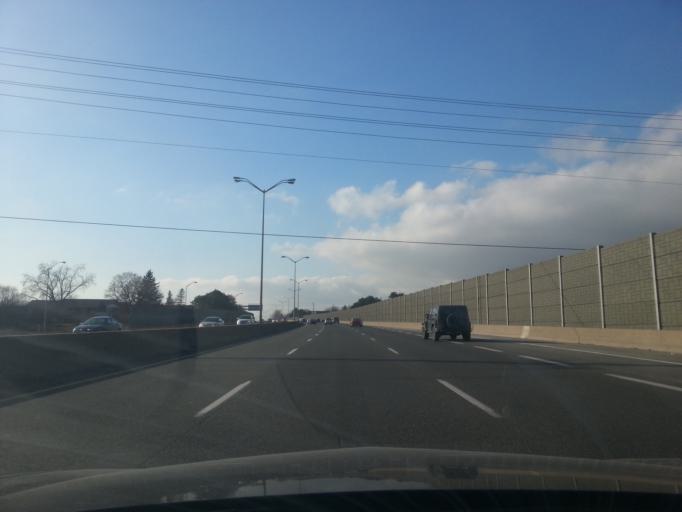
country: CA
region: Ontario
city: Oshawa
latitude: 43.8870
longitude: -78.8311
